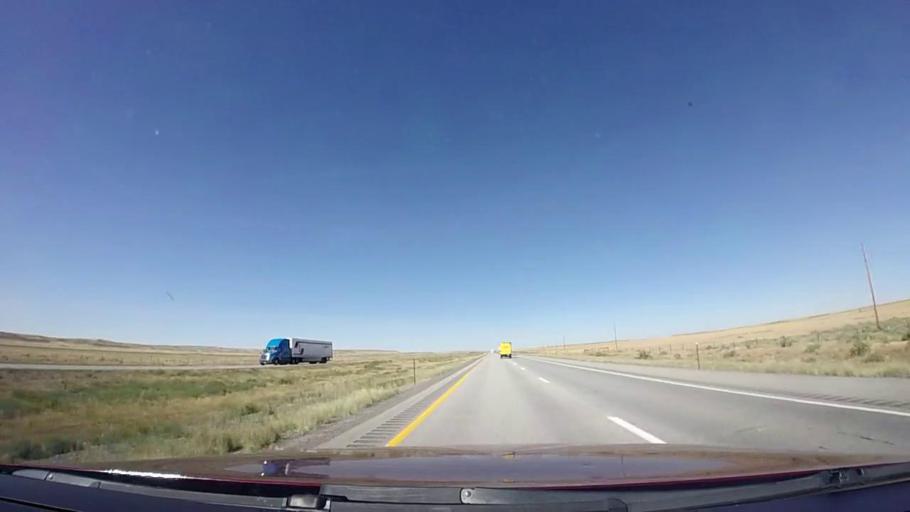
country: US
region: Wyoming
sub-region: Carbon County
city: Rawlins
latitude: 41.6638
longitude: -108.0441
